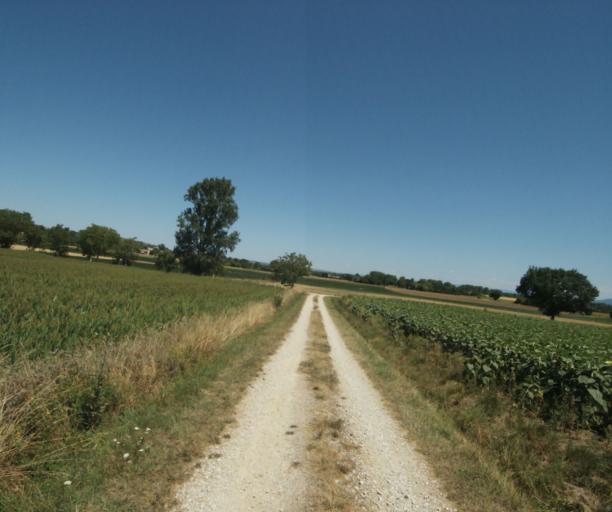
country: FR
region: Midi-Pyrenees
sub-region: Departement de la Haute-Garonne
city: Saint-Felix-Lauragais
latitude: 43.4703
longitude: 1.9237
